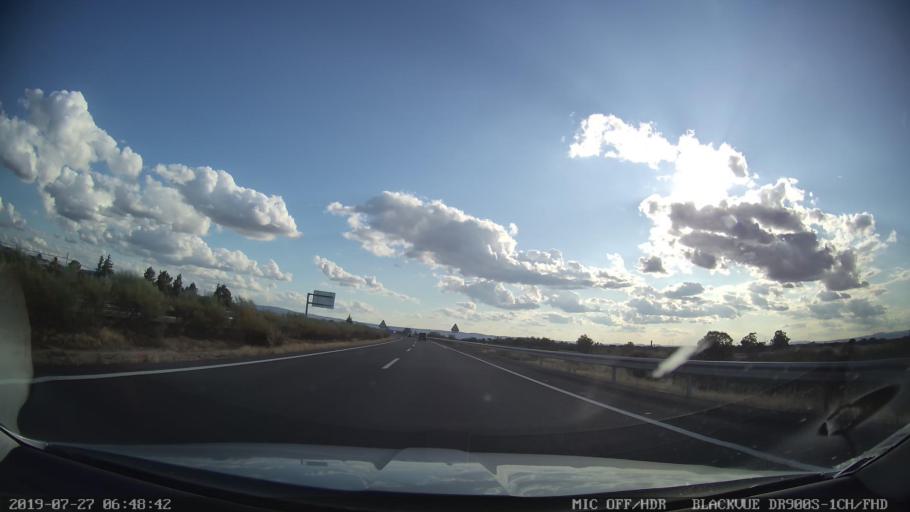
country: ES
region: Extremadura
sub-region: Provincia de Caceres
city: Millanes
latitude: 39.8639
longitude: -5.6063
